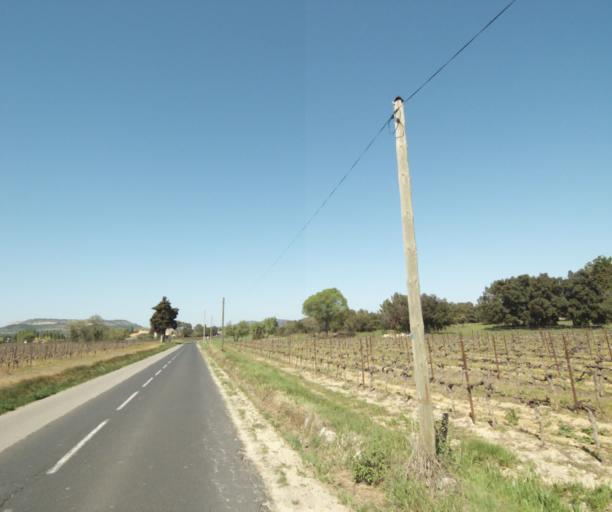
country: FR
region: Languedoc-Roussillon
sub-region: Departement de l'Herault
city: Saint-Drezery
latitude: 43.7426
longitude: 3.9590
